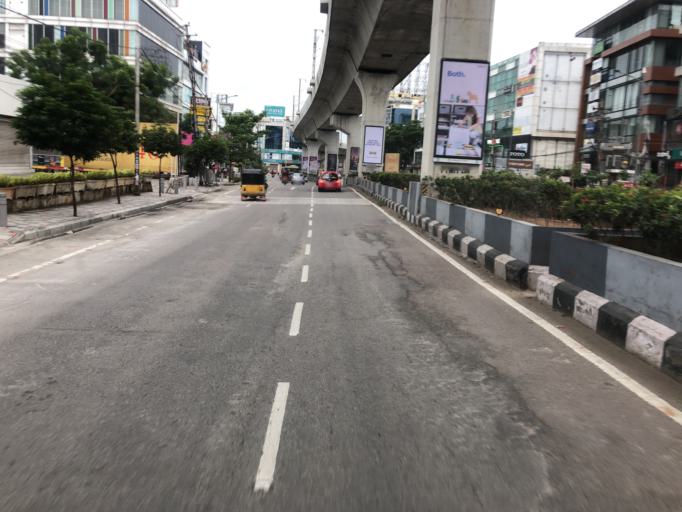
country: IN
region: Telangana
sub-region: Rangareddi
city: Kukatpalli
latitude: 17.4348
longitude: 78.4029
